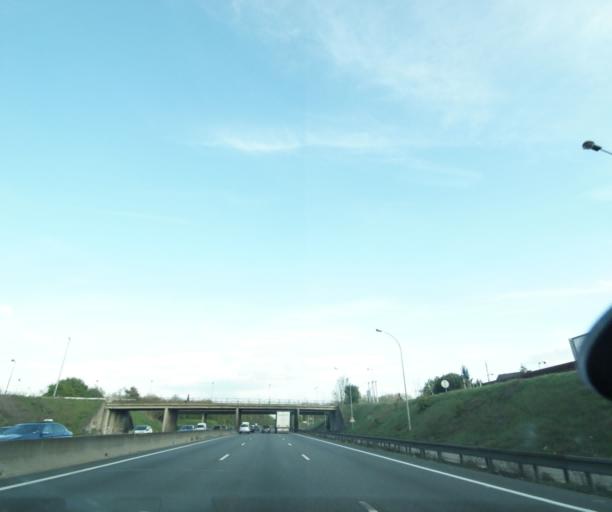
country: FR
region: Ile-de-France
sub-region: Departement de l'Essonne
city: Morsang-sur-Orge
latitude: 48.6603
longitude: 2.3720
